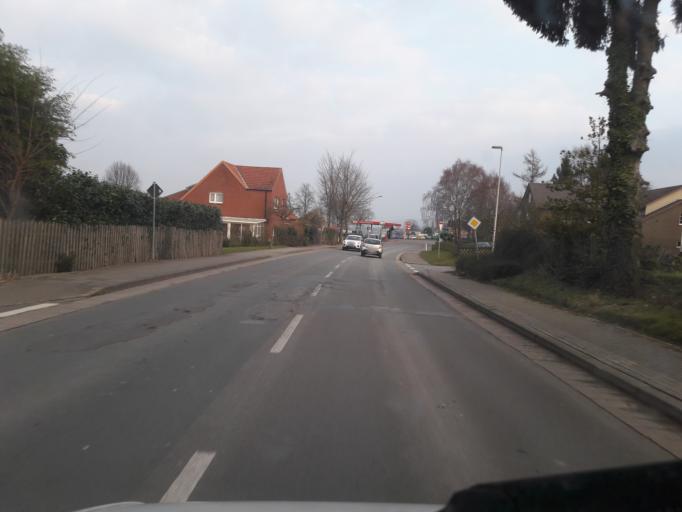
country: DE
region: North Rhine-Westphalia
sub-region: Regierungsbezirk Detmold
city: Hille
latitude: 52.2843
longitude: 8.7539
